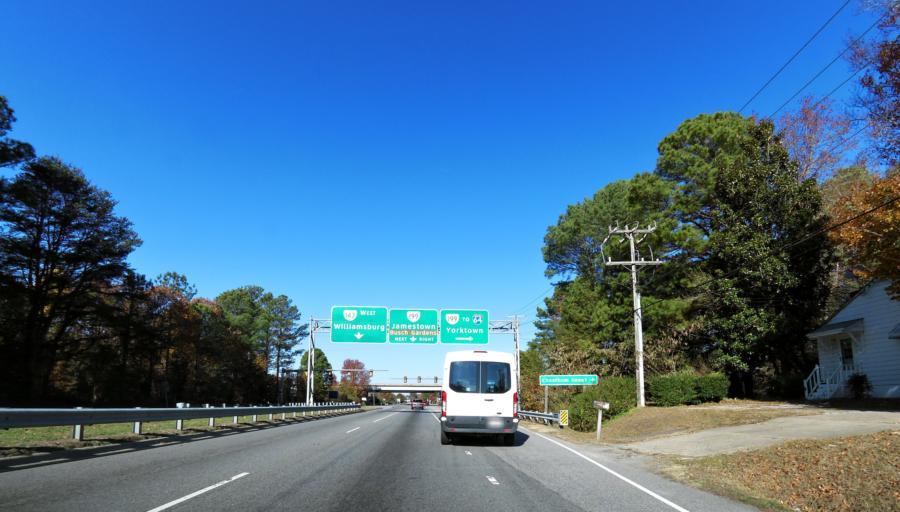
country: US
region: Virginia
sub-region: City of Williamsburg
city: Williamsburg
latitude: 37.2505
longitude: -76.6602
